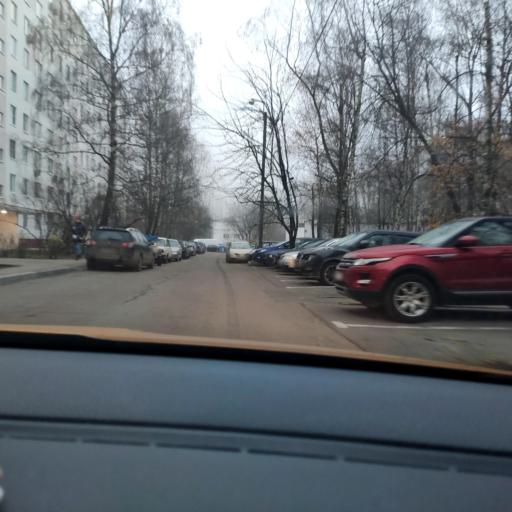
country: RU
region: Moscow
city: Tyoply Stan
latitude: 55.6287
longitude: 37.5104
